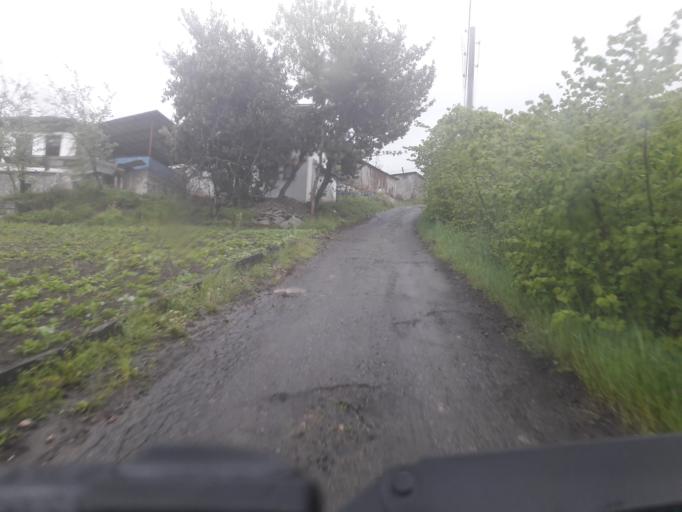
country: TR
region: Trabzon
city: Duzkoy
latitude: 40.9298
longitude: 39.4812
